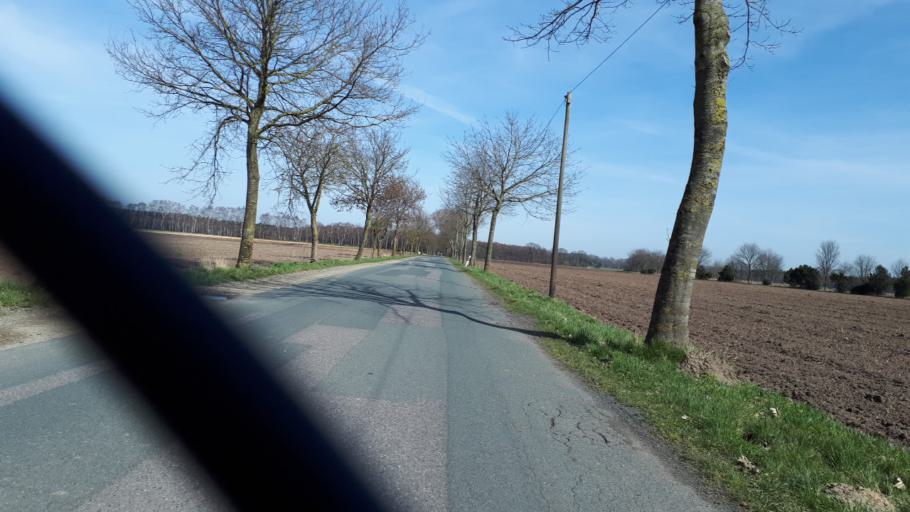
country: DE
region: Lower Saxony
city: Cloppenburg
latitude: 52.8775
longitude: 8.0000
